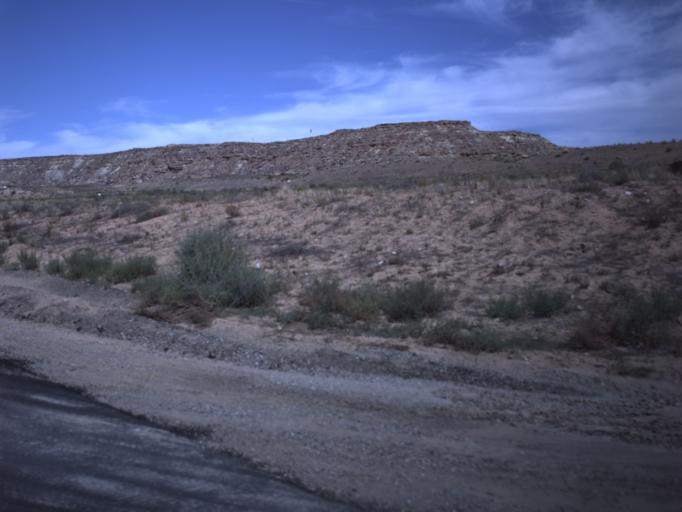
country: US
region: Utah
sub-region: San Juan County
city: Blanding
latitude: 37.2283
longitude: -109.2124
